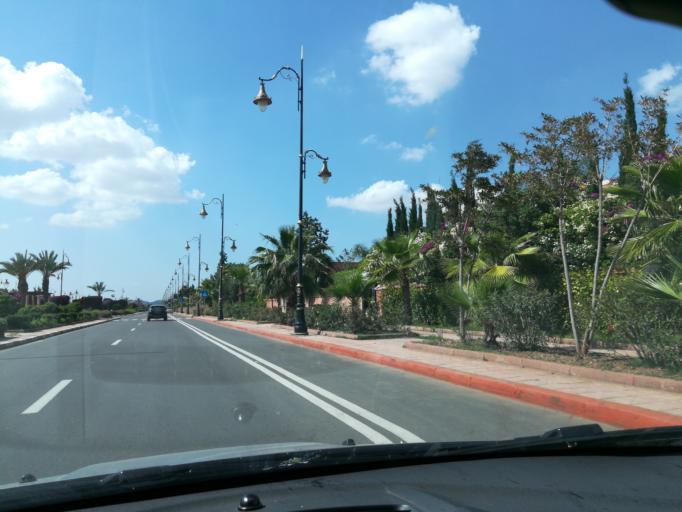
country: MA
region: Marrakech-Tensift-Al Haouz
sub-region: Marrakech
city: Marrakesh
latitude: 31.6057
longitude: -7.9998
